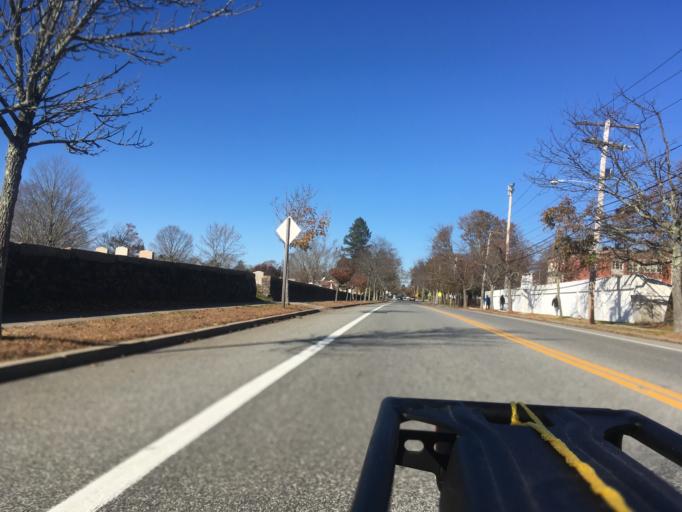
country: US
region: Rhode Island
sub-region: Kent County
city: East Greenwich
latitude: 41.6561
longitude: -71.4554
